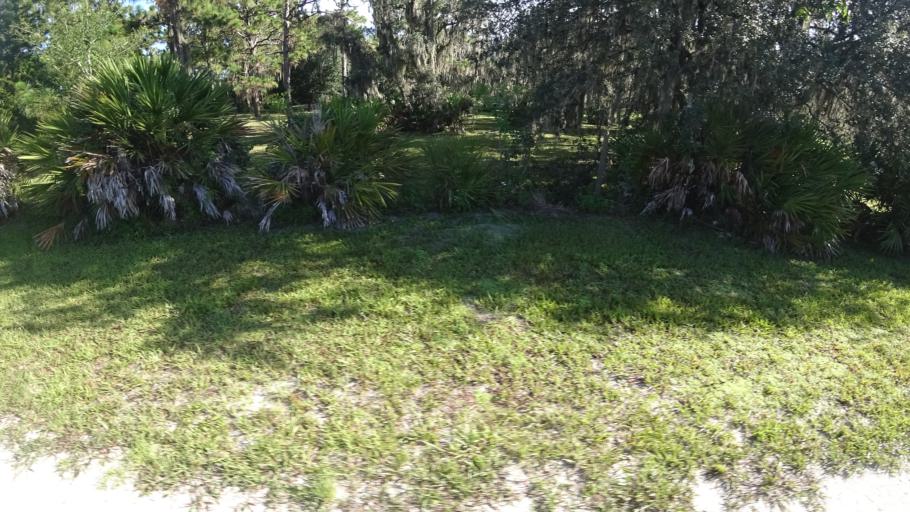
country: US
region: Florida
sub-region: Sarasota County
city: The Meadows
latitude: 27.4194
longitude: -82.2634
